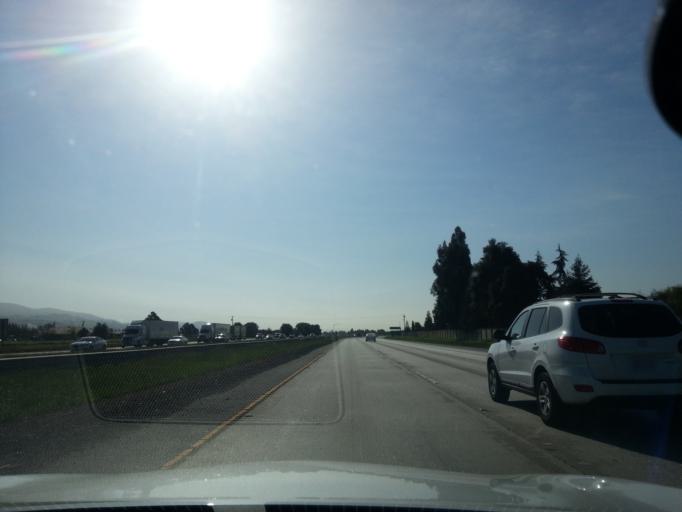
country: US
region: California
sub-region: Santa Clara County
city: Morgan Hill
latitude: 37.1391
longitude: -121.6393
